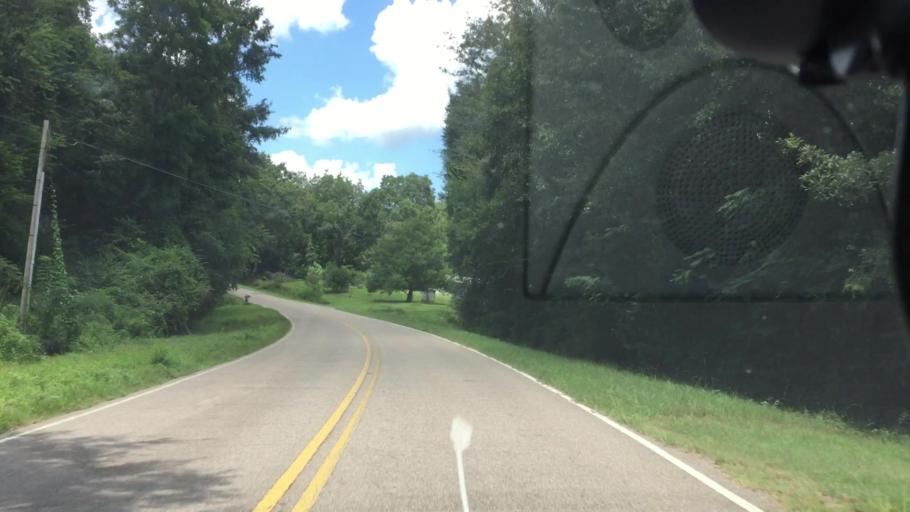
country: US
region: Alabama
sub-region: Coffee County
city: Enterprise
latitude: 31.3987
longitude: -85.8314
